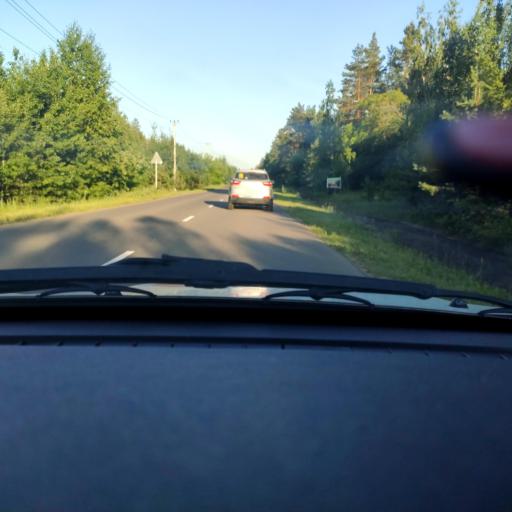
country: RU
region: Voronezj
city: Ramon'
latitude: 51.8909
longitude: 39.2454
